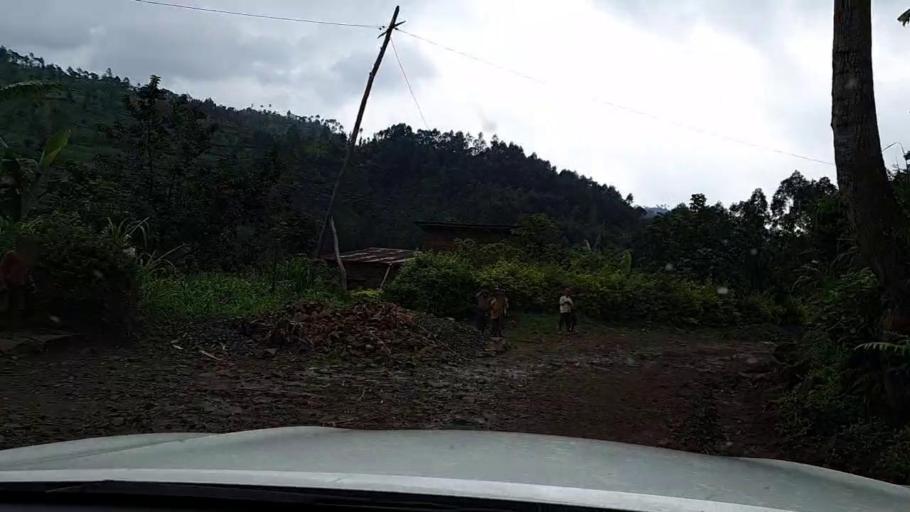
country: RW
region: Western Province
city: Cyangugu
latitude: -2.5392
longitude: 29.0392
